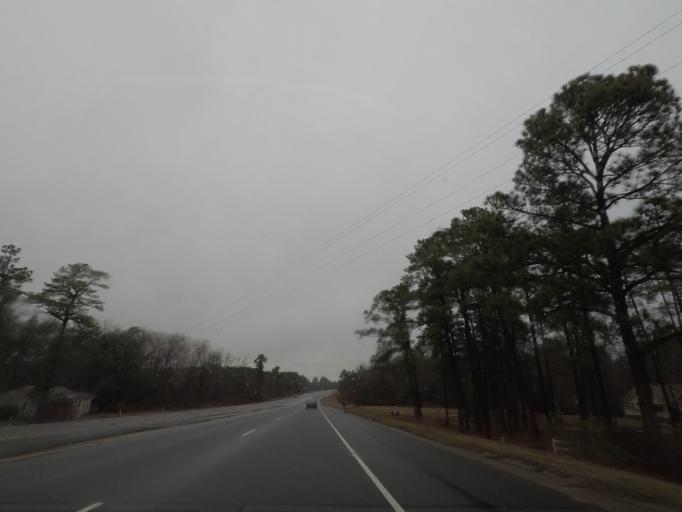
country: US
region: North Carolina
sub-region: Lee County
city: Broadway
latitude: 35.3477
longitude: -79.1073
